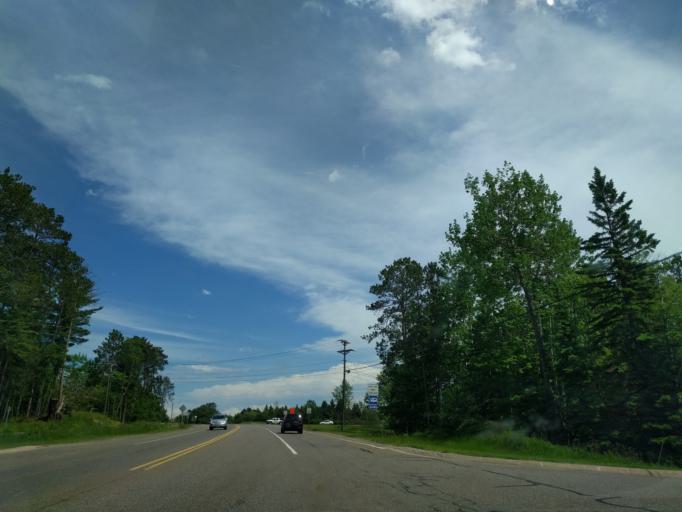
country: US
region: Michigan
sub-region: Marquette County
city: Marquette
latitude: 46.5718
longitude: -87.4090
